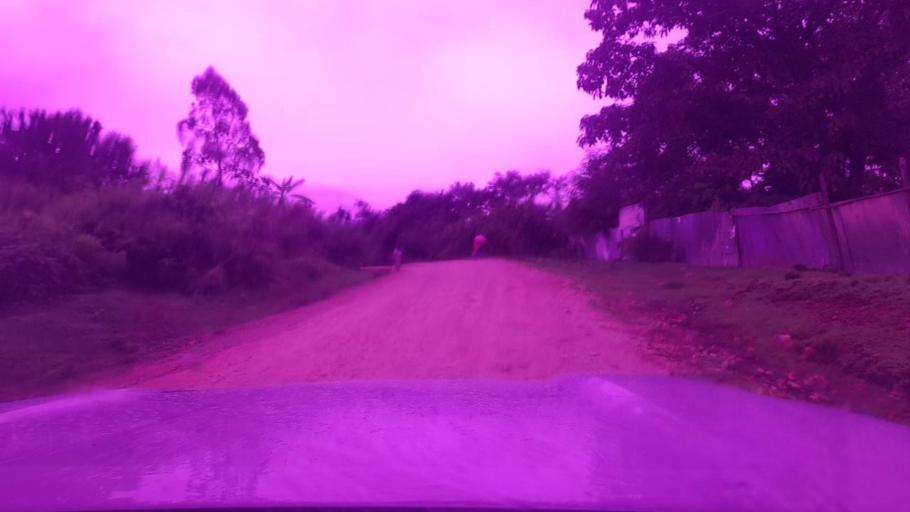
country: ET
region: Southern Nations, Nationalities, and People's Region
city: Bonga
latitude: 7.4494
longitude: 36.1307
